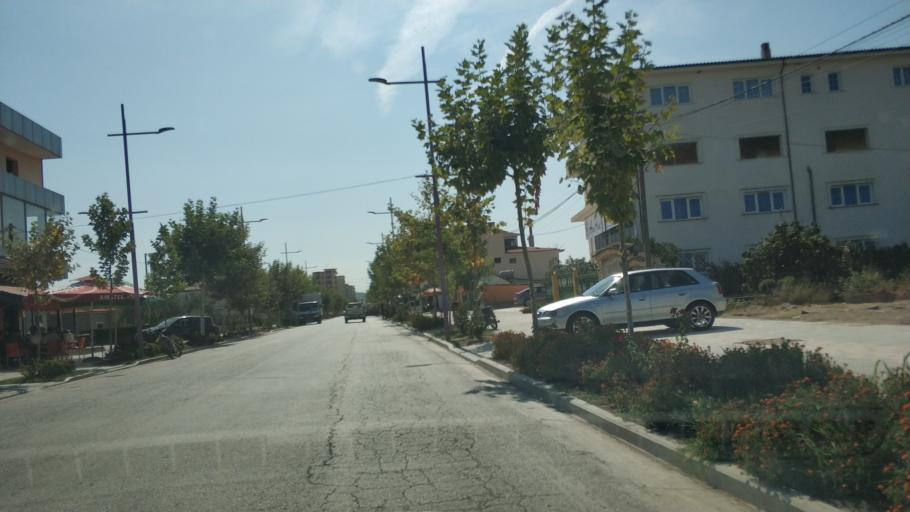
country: AL
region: Fier
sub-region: Rrethi i Lushnjes
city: Divjake
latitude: 41.0026
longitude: 19.5301
